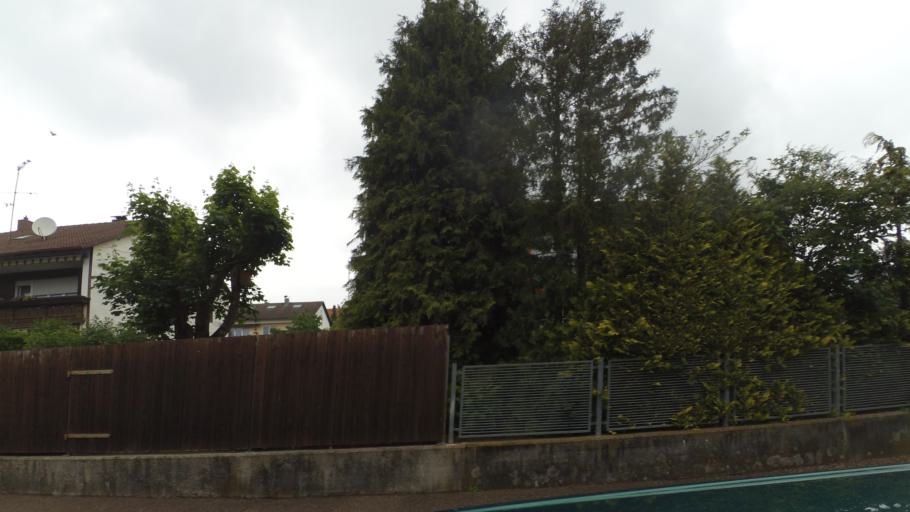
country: DE
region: Bavaria
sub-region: Swabia
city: Monheim
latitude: 48.8432
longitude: 10.8610
